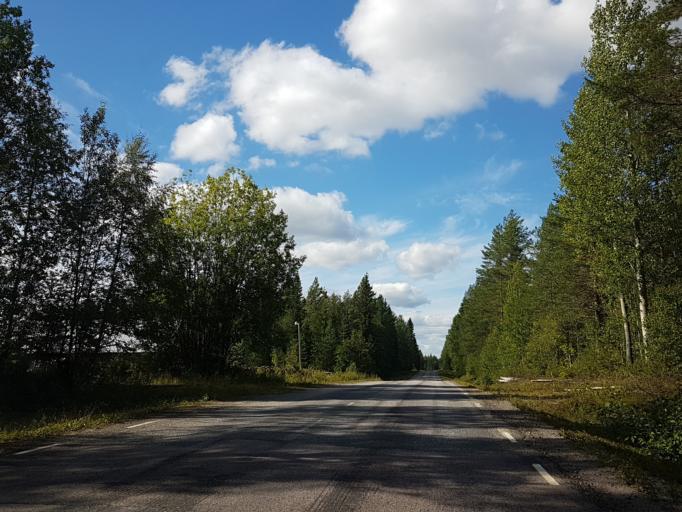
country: SE
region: Vaesterbotten
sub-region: Umea Kommun
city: Saevar
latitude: 64.2099
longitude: 20.4904
